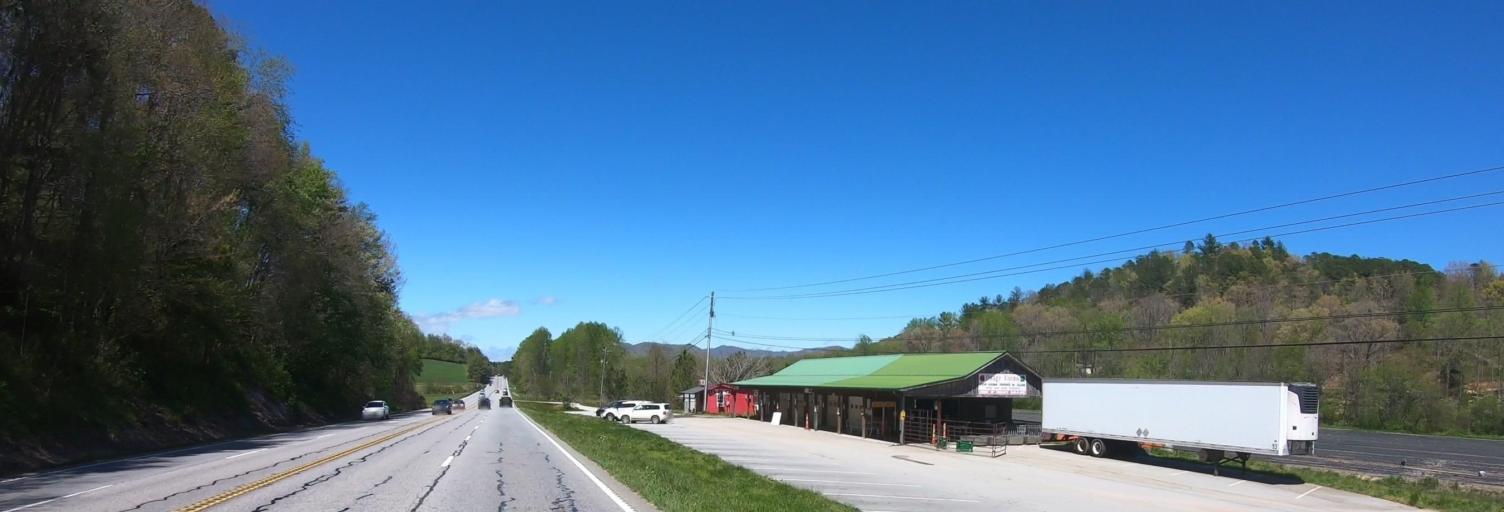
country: US
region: Georgia
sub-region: Rabun County
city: Mountain City
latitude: 34.9480
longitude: -83.3870
